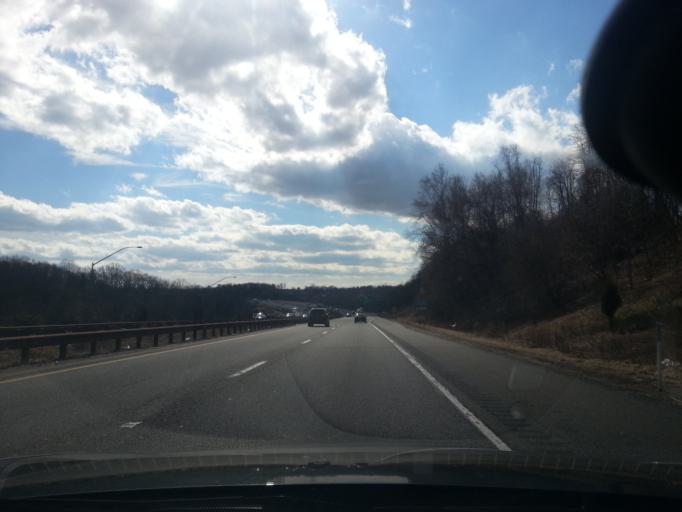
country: US
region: Pennsylvania
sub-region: Delaware County
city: Springfield
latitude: 39.9415
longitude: -75.3576
